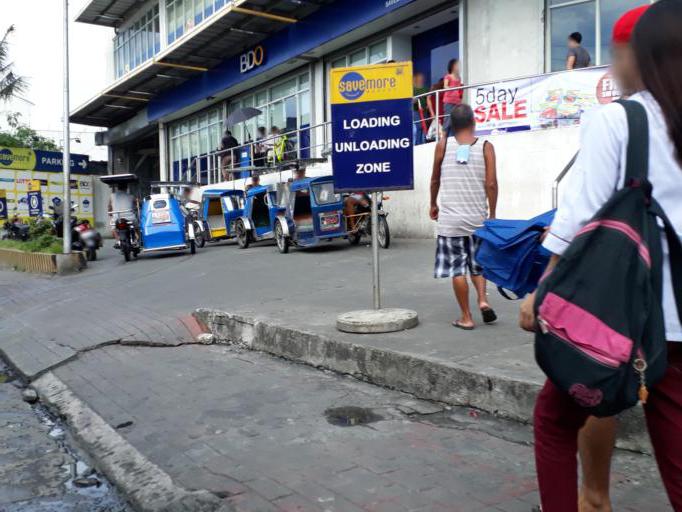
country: PH
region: Metro Manila
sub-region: Caloocan City
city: Niugan
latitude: 14.6743
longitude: 120.9828
